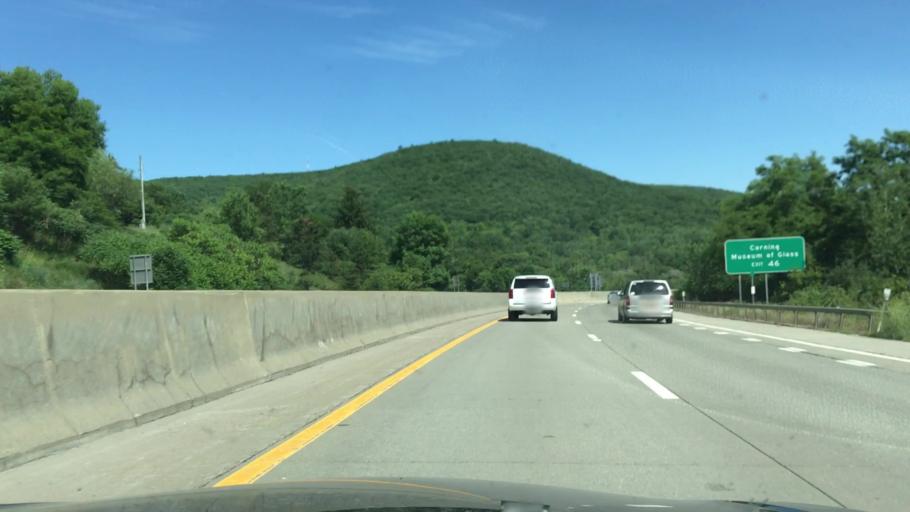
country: US
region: New York
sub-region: Steuben County
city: Corning
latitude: 42.1631
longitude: -77.0613
